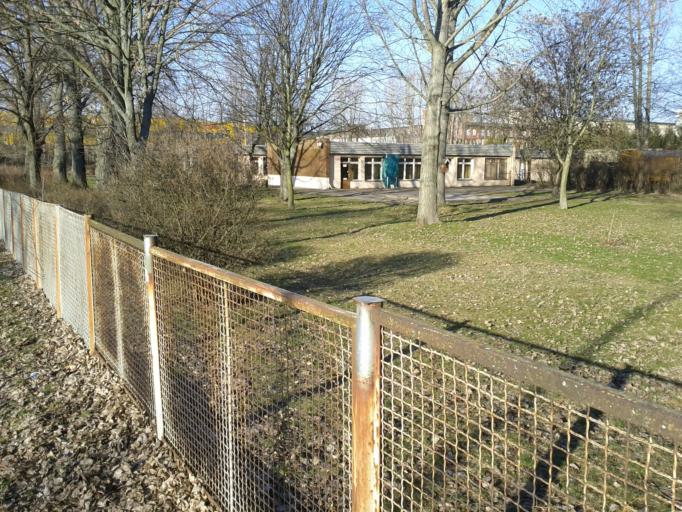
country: DE
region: Berlin
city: Lichtenberg
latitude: 52.5205
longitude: 13.4949
